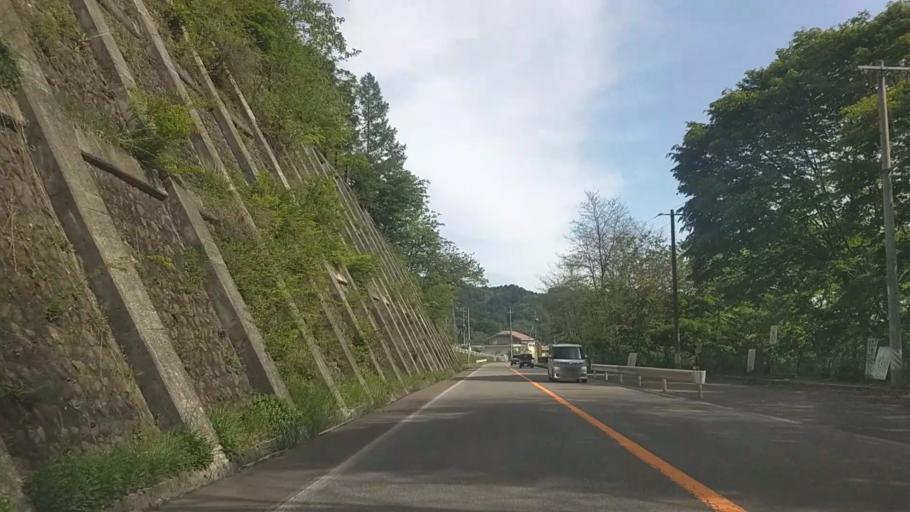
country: JP
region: Nagano
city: Saku
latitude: 36.0542
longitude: 138.4673
